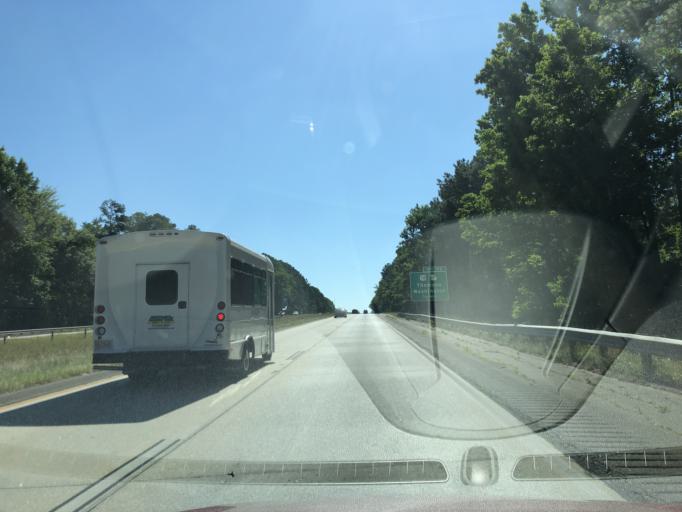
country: US
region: Georgia
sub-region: McDuffie County
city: Thomson
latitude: 33.5096
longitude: -82.5165
